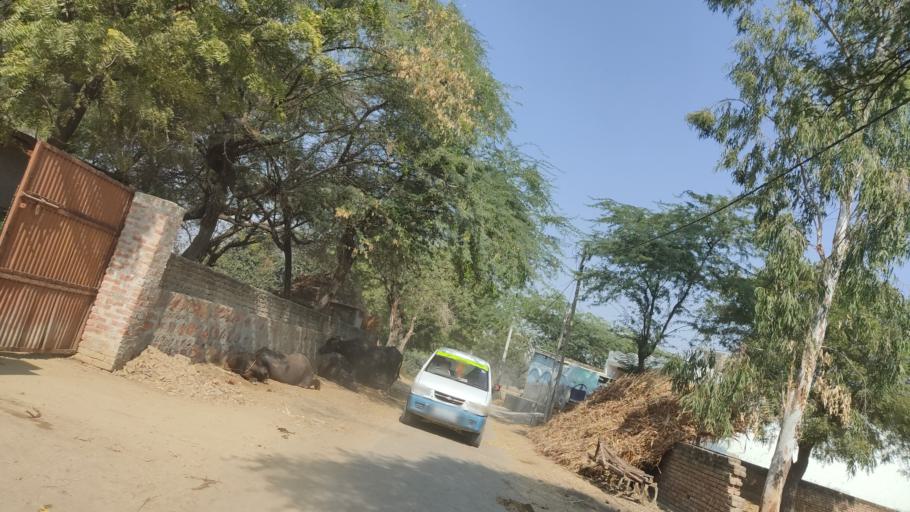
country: IN
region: Uttar Pradesh
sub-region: Mathura
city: Radha Kund
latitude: 27.5119
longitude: 77.4974
